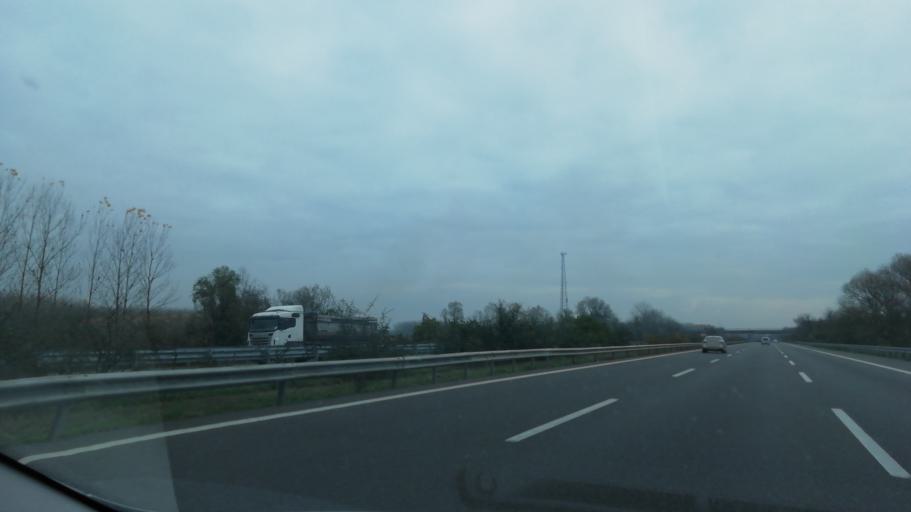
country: TR
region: Duzce
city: Duzce
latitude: 40.8122
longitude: 31.1105
